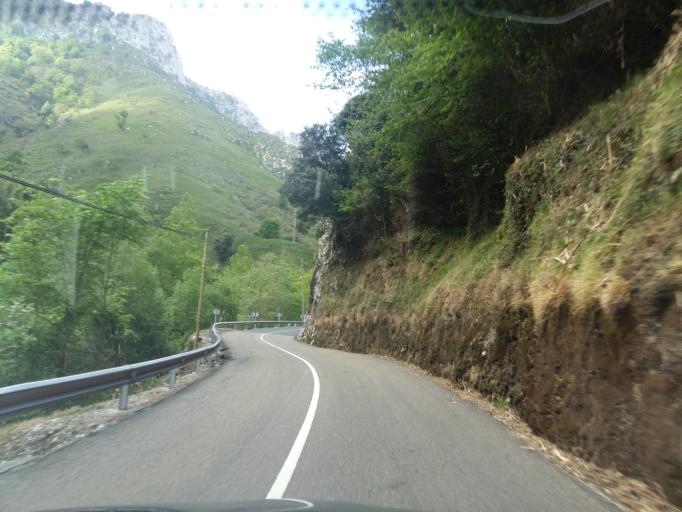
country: ES
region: Cantabria
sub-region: Provincia de Cantabria
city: Tresviso
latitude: 43.2808
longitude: -4.6285
